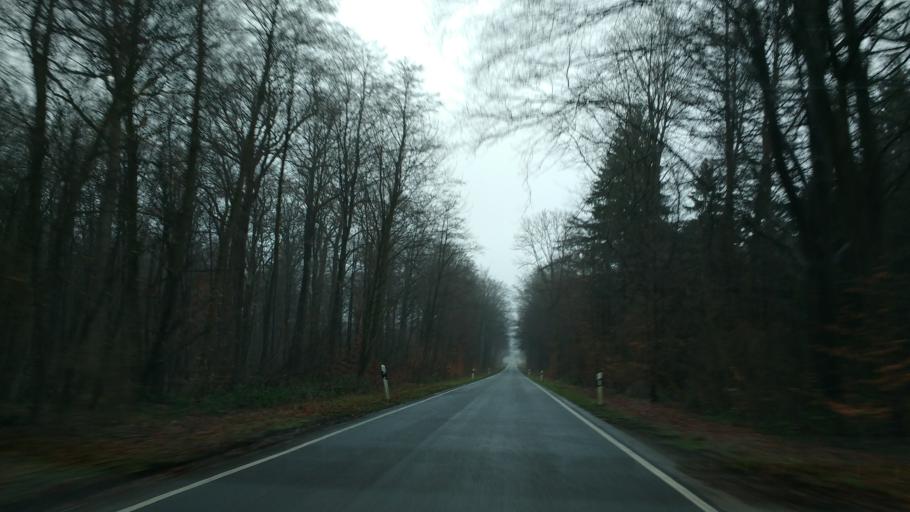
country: DE
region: Schleswig-Holstein
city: Nindorf
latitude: 54.1478
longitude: 9.6981
